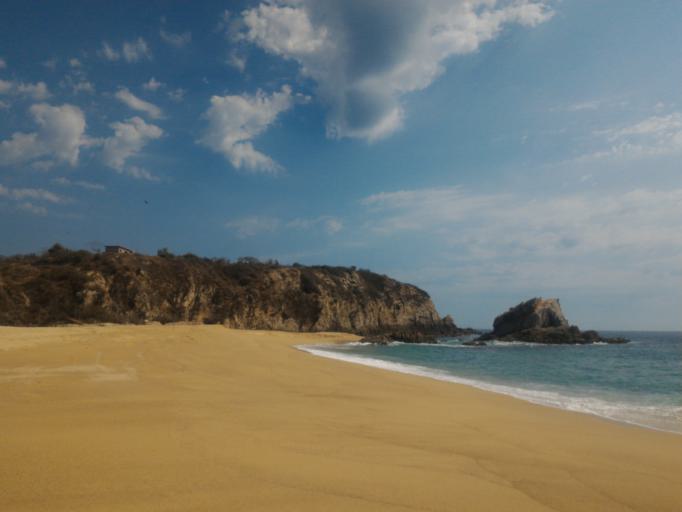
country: MX
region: Michoacan
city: Coahuayana Viejo
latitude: 18.2941
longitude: -103.4100
